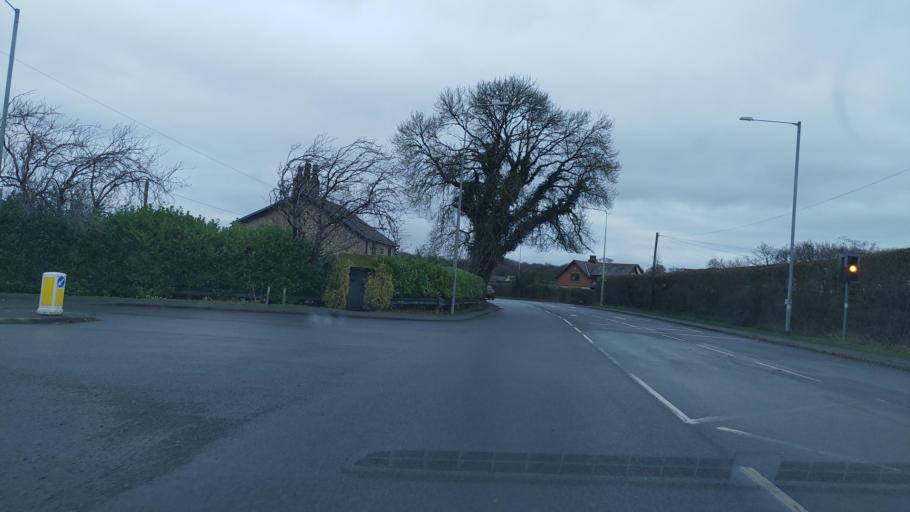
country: GB
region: England
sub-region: Lancashire
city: Clayton-le-Woods
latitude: 53.7057
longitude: -2.6715
